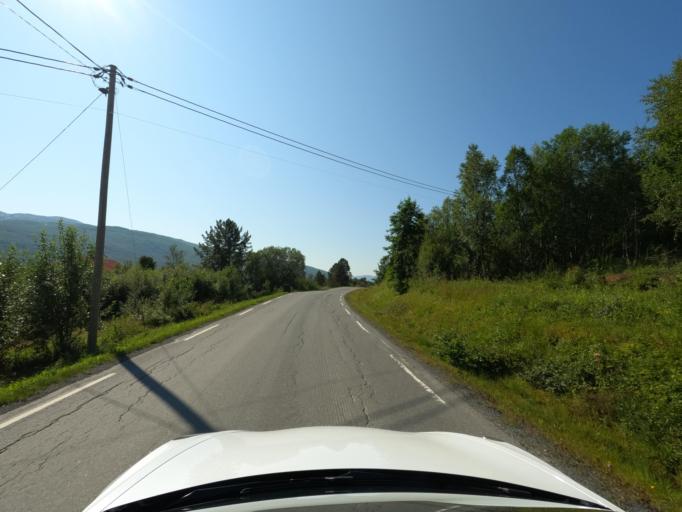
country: NO
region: Nordland
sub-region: Ballangen
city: Ballangen
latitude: 68.3515
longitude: 16.8606
